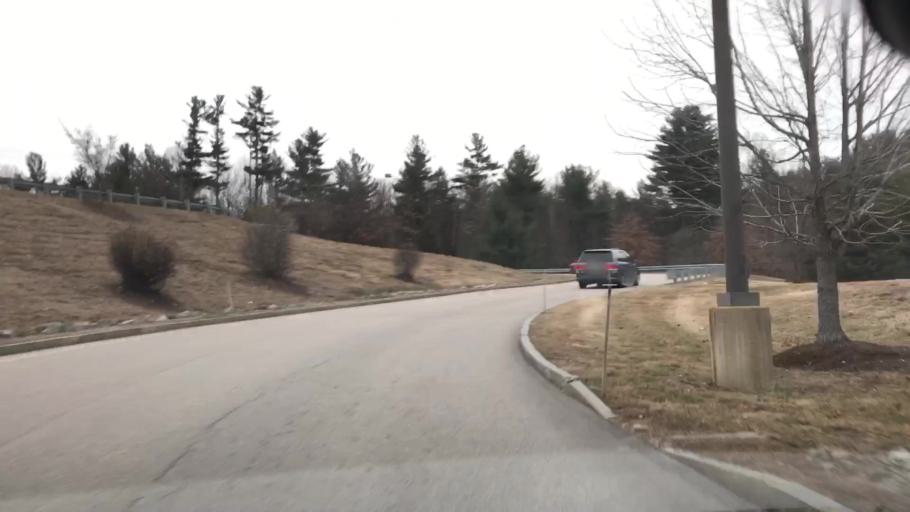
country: US
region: New Hampshire
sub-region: Hillsborough County
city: Hollis
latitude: 42.8059
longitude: -71.5496
